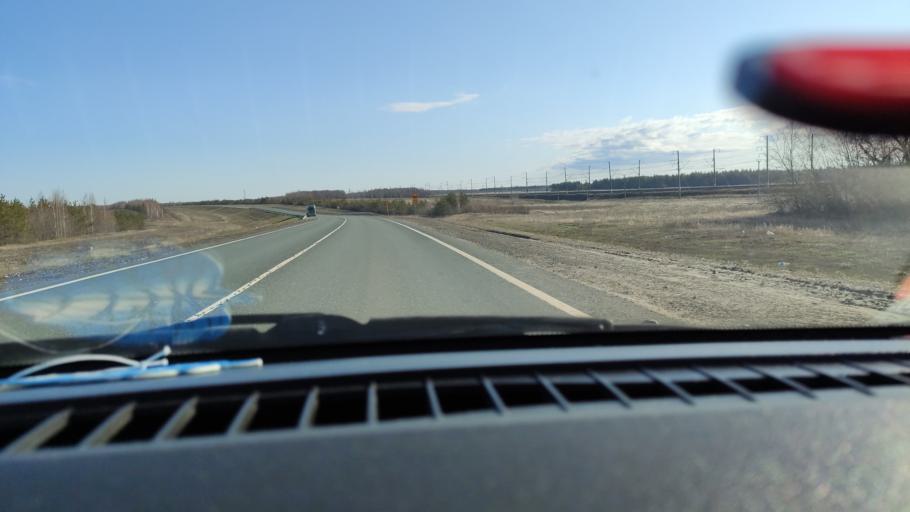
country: RU
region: Samara
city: Syzran'
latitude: 52.8732
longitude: 48.2872
